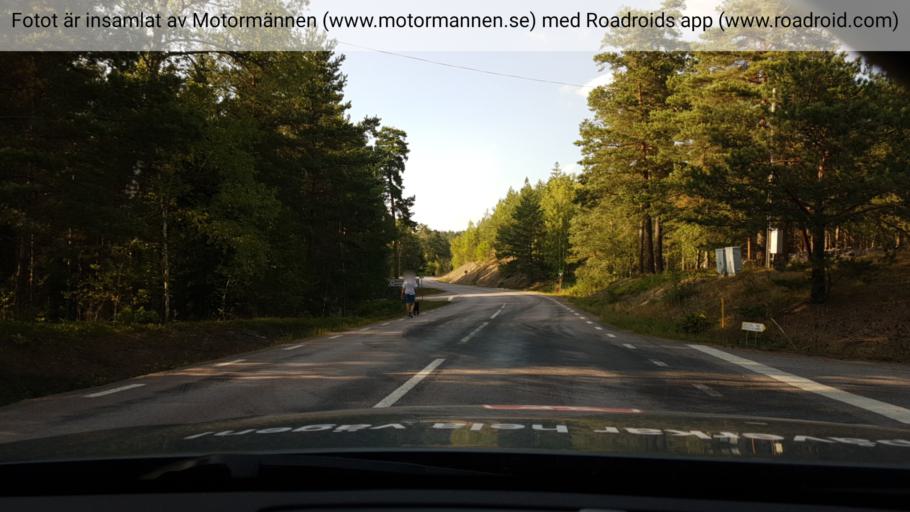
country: SE
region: Soedermanland
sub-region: Strangnas Kommun
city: Mariefred
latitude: 59.1692
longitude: 17.1858
